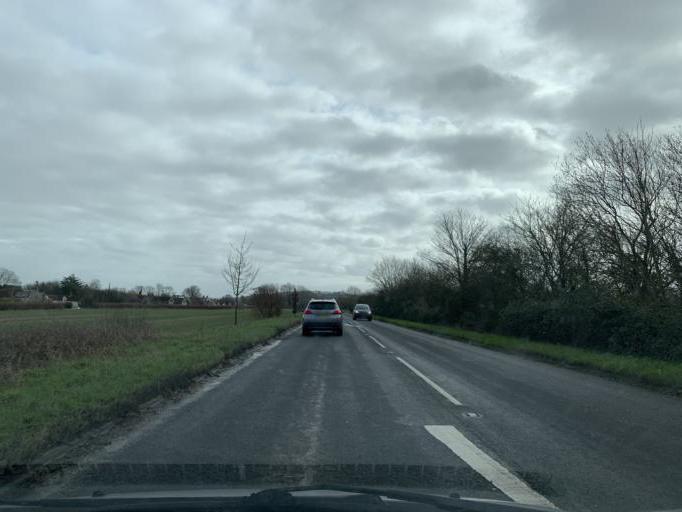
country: GB
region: England
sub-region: Wiltshire
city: Wilton
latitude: 51.0668
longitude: -1.8475
